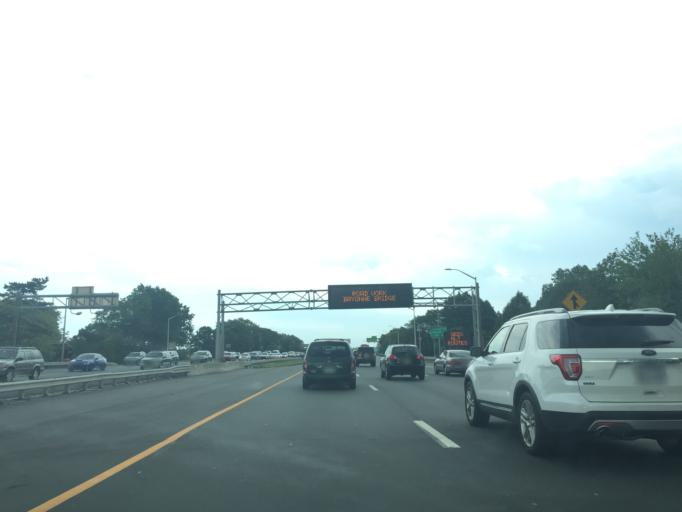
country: US
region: New York
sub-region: Richmond County
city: Bloomfield
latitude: 40.6170
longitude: -74.1600
